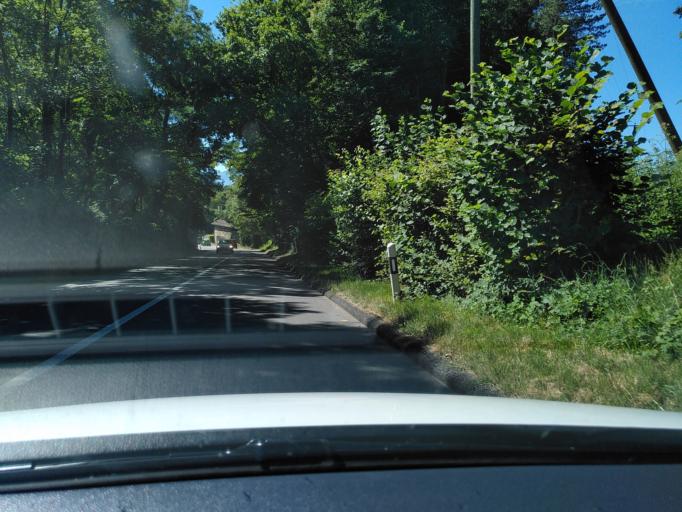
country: CH
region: Vaud
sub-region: Morges District
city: Aubonne
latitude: 46.4745
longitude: 6.4055
